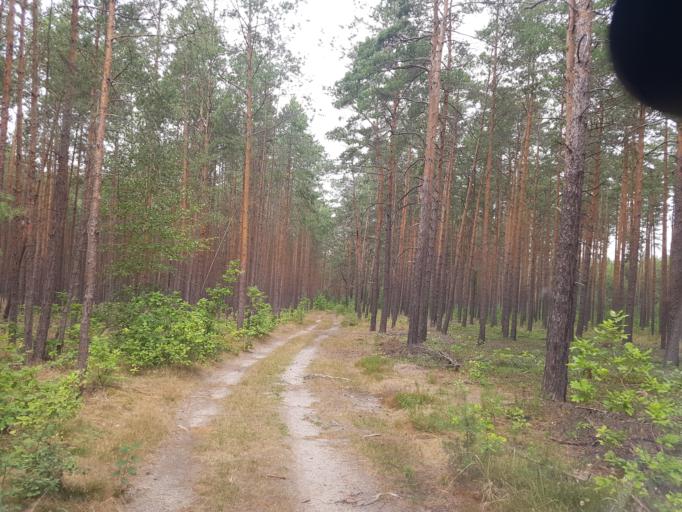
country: DE
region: Brandenburg
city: Finsterwalde
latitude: 51.6441
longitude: 13.6738
